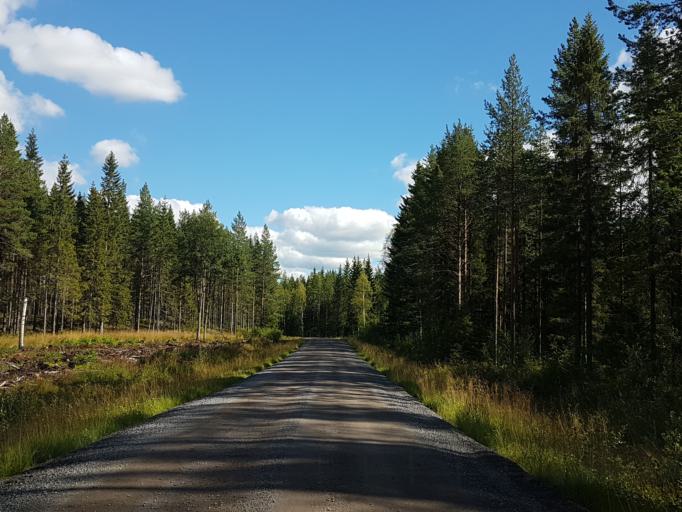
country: SE
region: Vaesterbotten
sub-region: Skelleftea Kommun
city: Burtraesk
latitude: 64.2963
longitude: 20.4948
